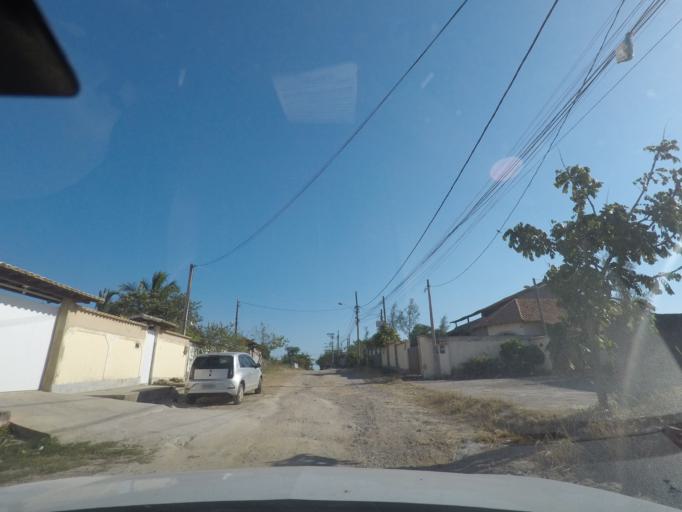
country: BR
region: Rio de Janeiro
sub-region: Marica
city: Marica
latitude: -22.9679
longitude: -42.9262
